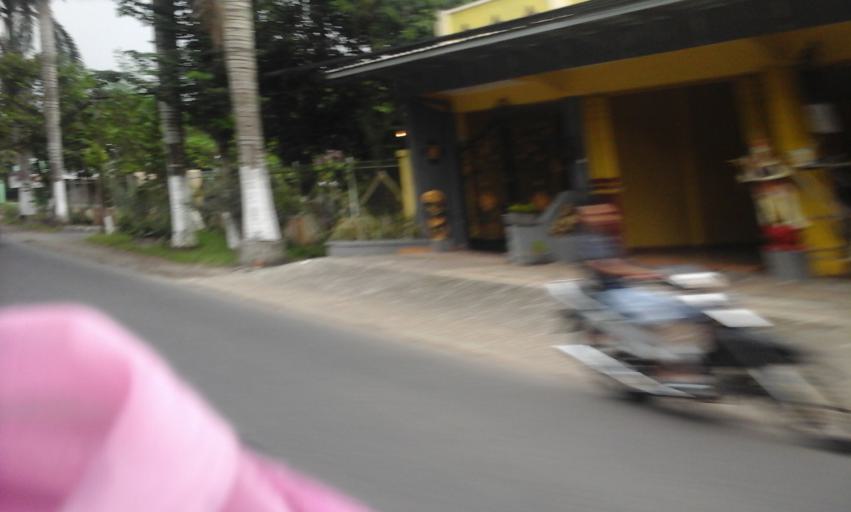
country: ID
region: East Java
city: Durenan
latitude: -8.2520
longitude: 113.6509
